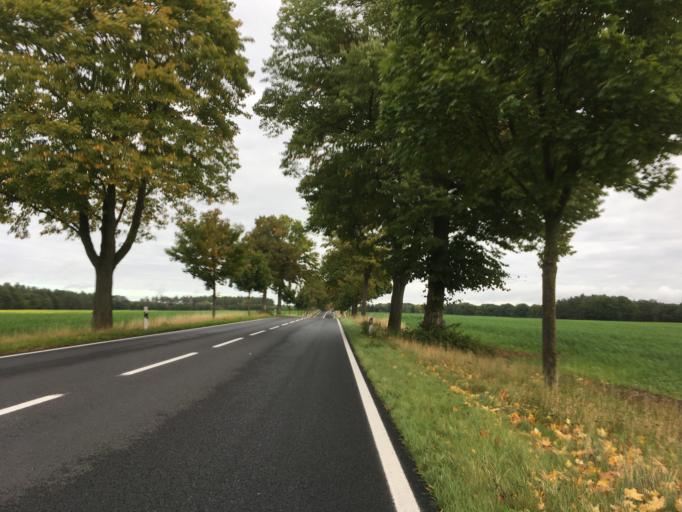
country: DE
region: Brandenburg
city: Werftpfuhl
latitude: 52.6940
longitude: 13.8647
